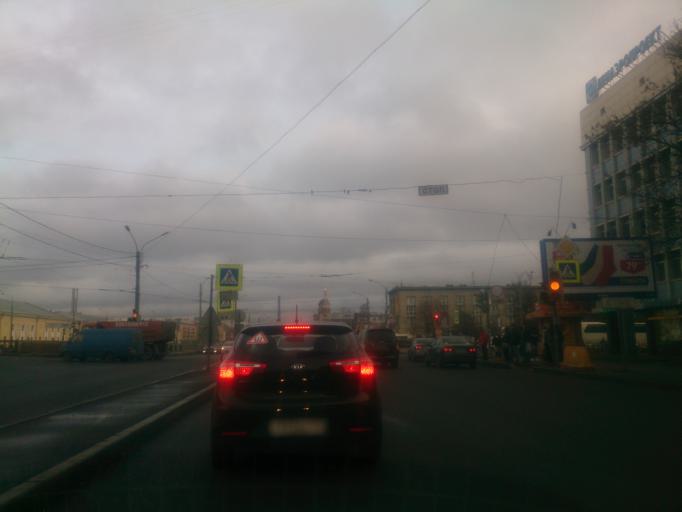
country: RU
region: St.-Petersburg
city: Admiralteisky
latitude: 59.9086
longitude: 30.2969
